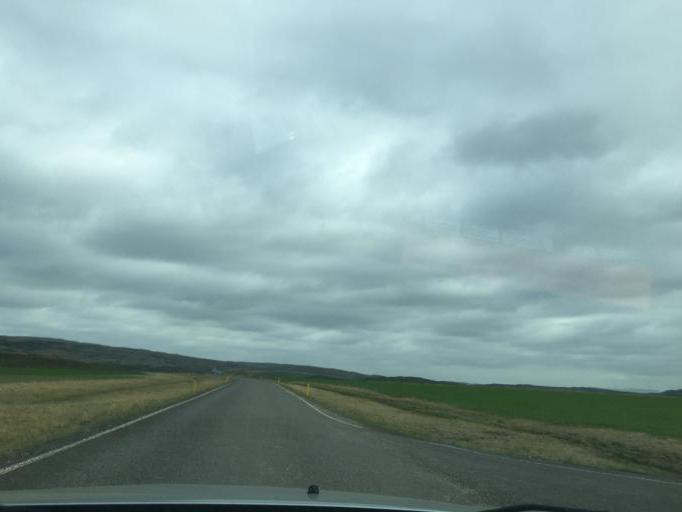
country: IS
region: South
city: Vestmannaeyjar
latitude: 64.2757
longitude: -20.2269
